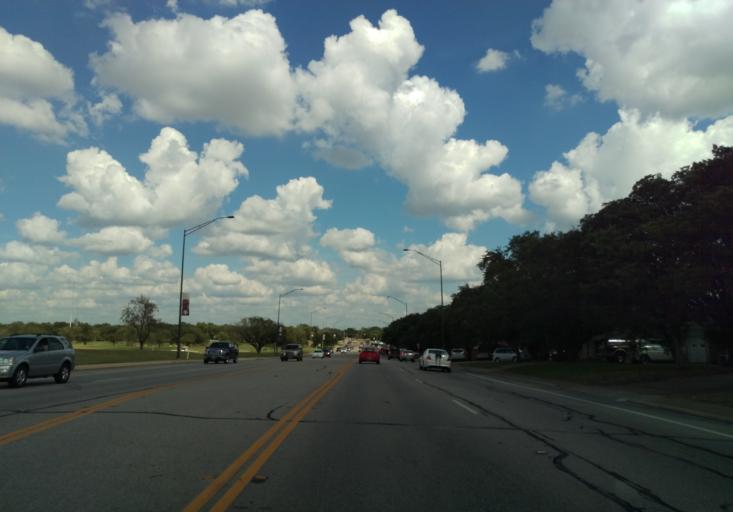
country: US
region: Texas
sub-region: Brazos County
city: College Station
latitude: 30.6158
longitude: -96.3267
